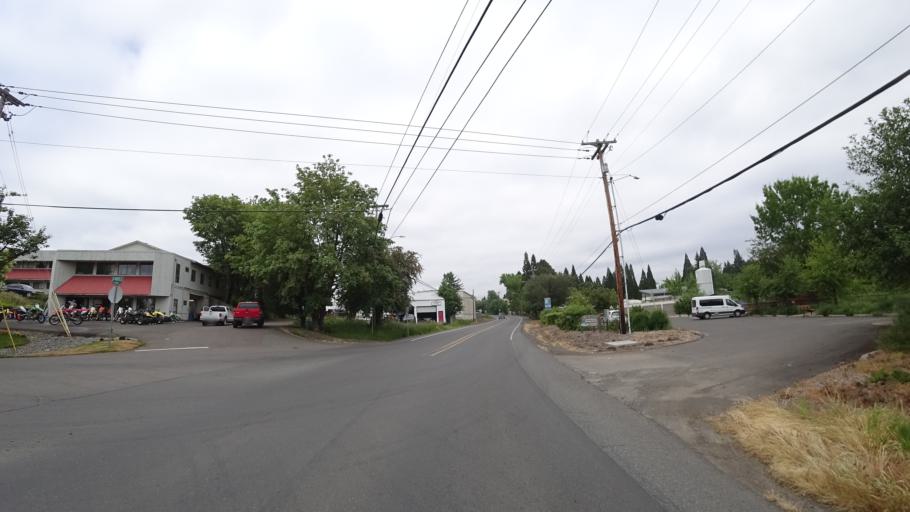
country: US
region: Oregon
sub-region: Washington County
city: Hillsboro
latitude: 45.5126
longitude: -122.9909
